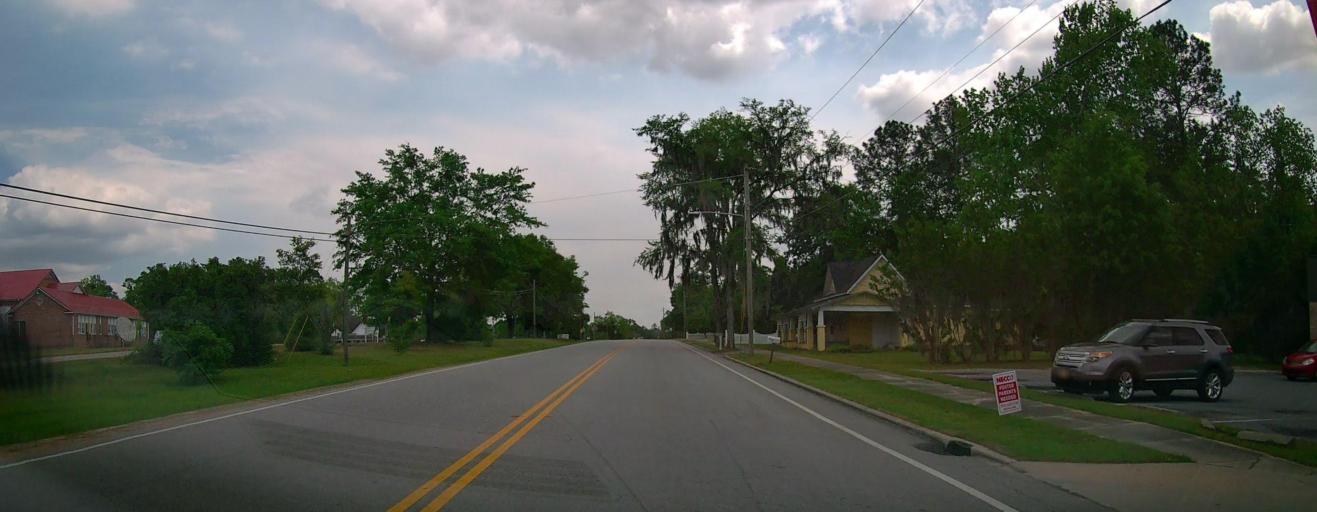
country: US
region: Georgia
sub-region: Treutlen County
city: Soperton
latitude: 32.3745
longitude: -82.5884
